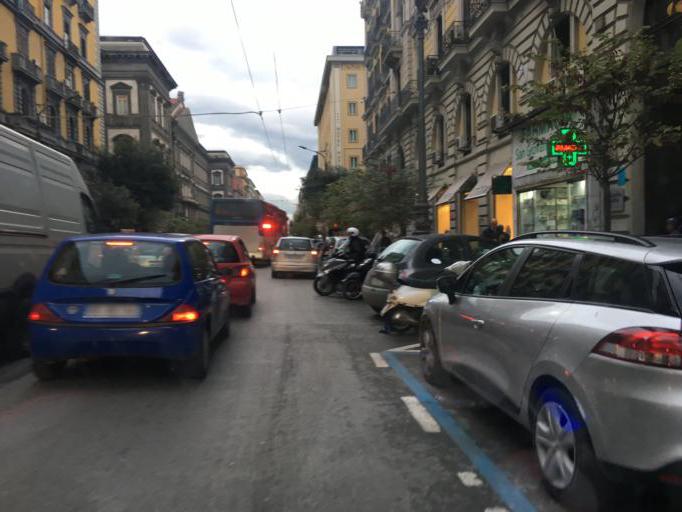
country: IT
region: Campania
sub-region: Provincia di Napoli
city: Napoli
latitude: 40.8444
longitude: 14.2567
